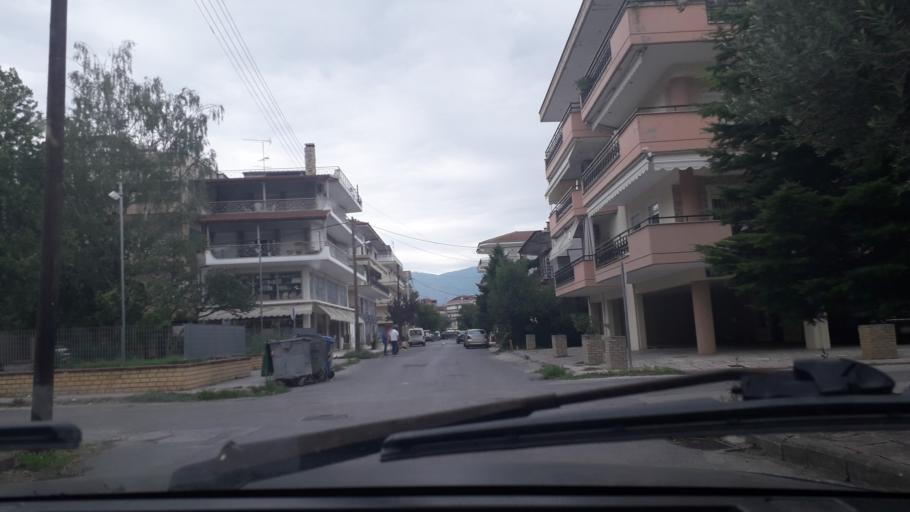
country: GR
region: Central Macedonia
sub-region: Nomos Pellis
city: Aridaia
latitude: 40.9708
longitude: 22.0632
